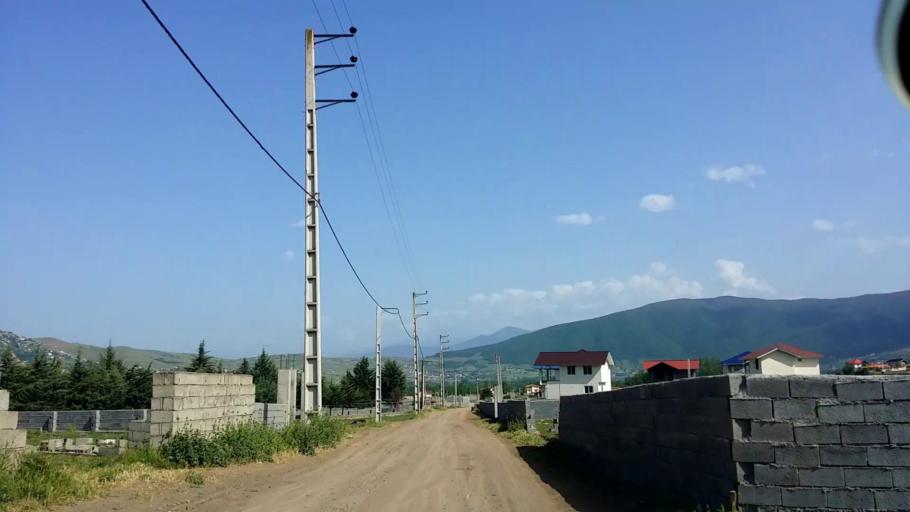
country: IR
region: Mazandaran
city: `Abbasabad
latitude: 36.5453
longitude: 51.1872
